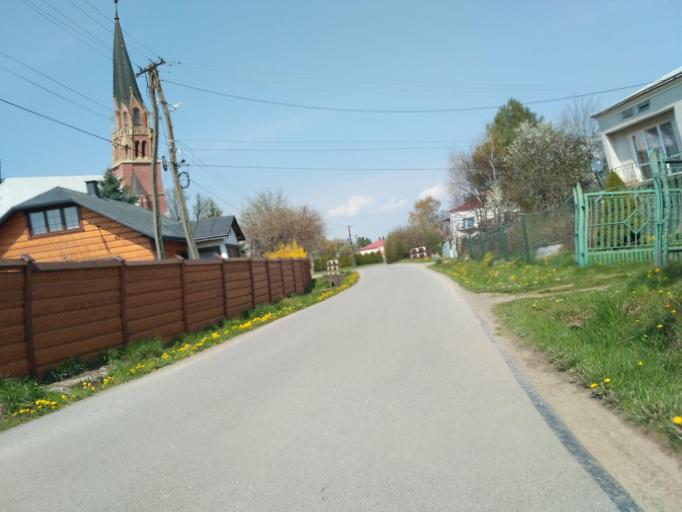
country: PL
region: Subcarpathian Voivodeship
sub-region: Powiat krosnienski
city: Chorkowka
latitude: 49.6284
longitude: 21.7032
